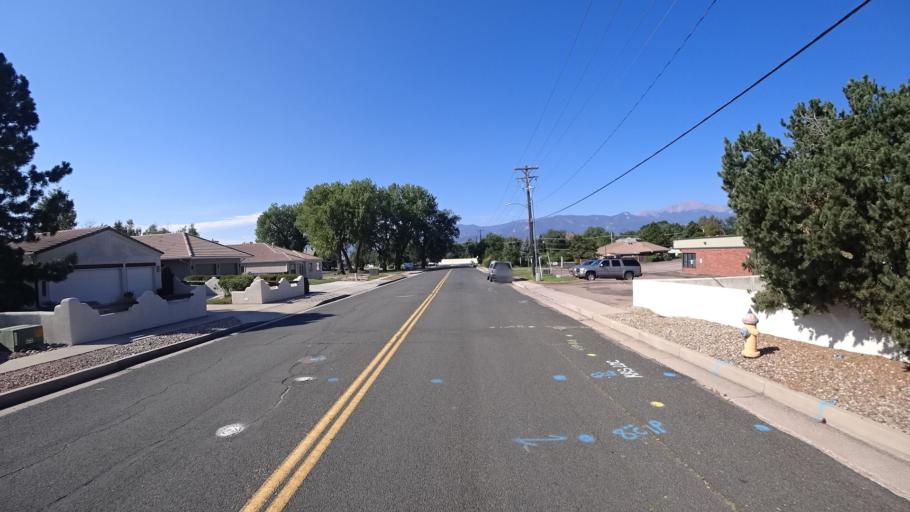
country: US
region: Colorado
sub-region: El Paso County
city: Colorado Springs
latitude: 38.8783
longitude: -104.7937
